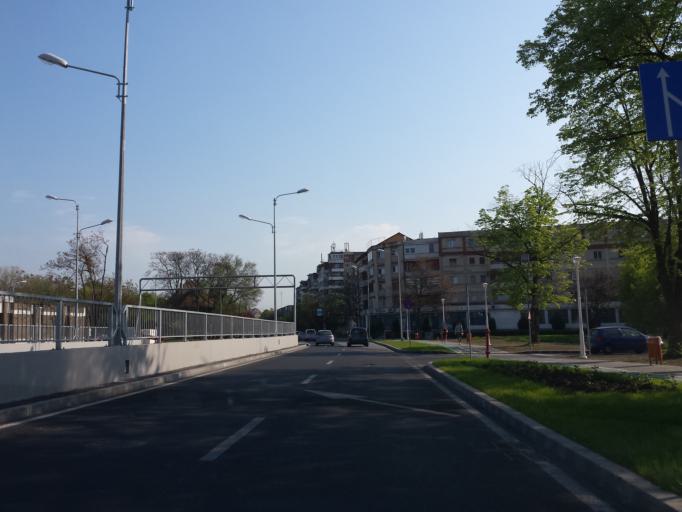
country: RO
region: Timis
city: Timisoara
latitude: 45.7498
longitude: 21.2373
